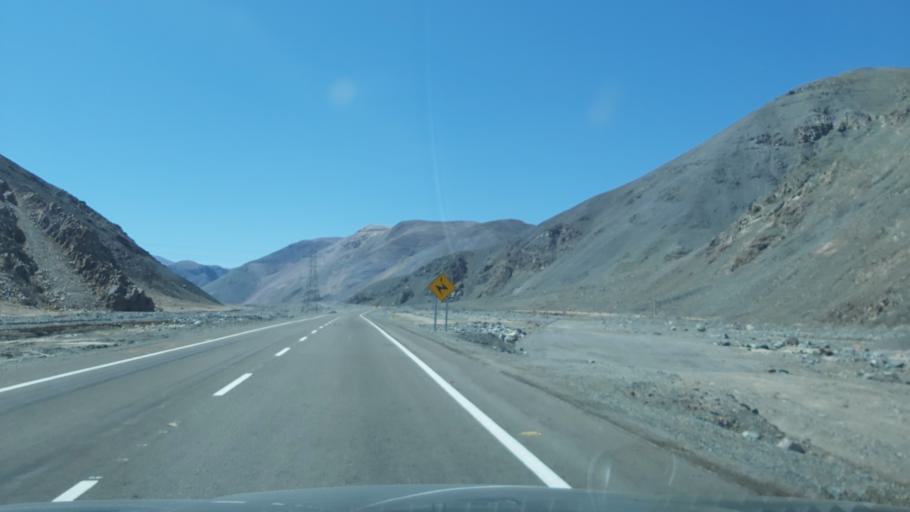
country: CL
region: Atacama
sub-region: Provincia de Chanaral
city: Diego de Almagro
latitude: -26.3514
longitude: -69.7349
